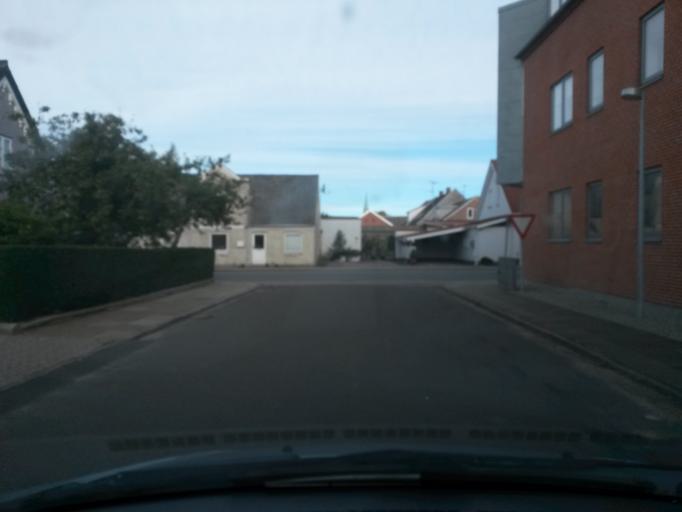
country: DK
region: Central Jutland
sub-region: Silkeborg Kommune
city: Kjellerup
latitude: 56.2906
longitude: 9.4294
